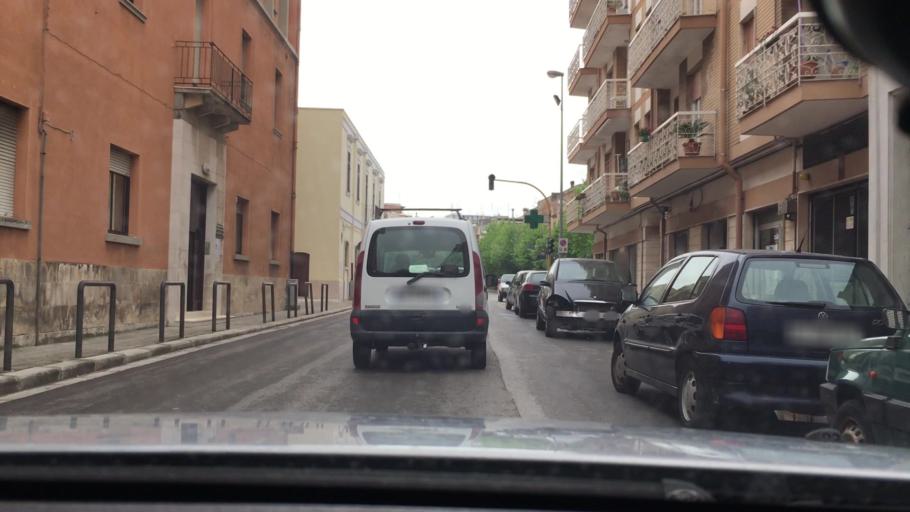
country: IT
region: Apulia
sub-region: Provincia di Bari
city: Gioia del Colle
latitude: 40.8042
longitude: 16.9235
